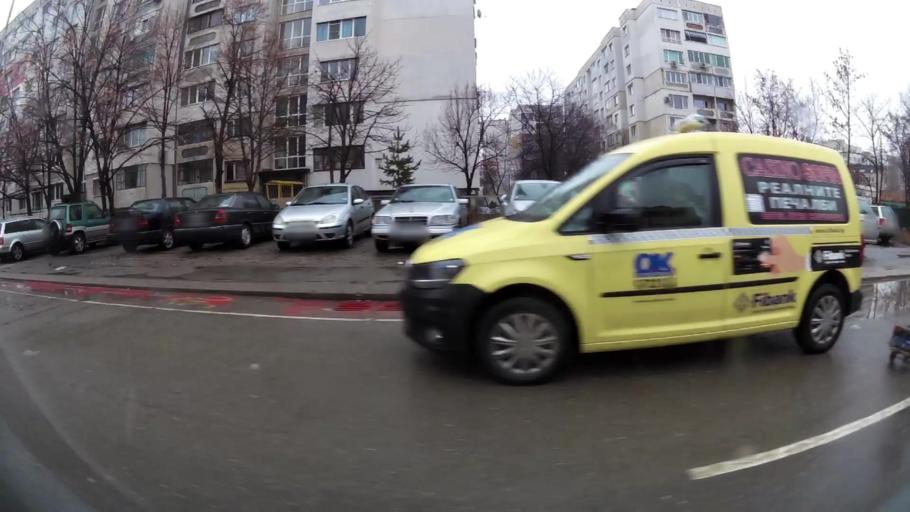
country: BG
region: Sofia-Capital
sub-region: Stolichna Obshtina
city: Sofia
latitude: 42.6312
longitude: 23.3750
